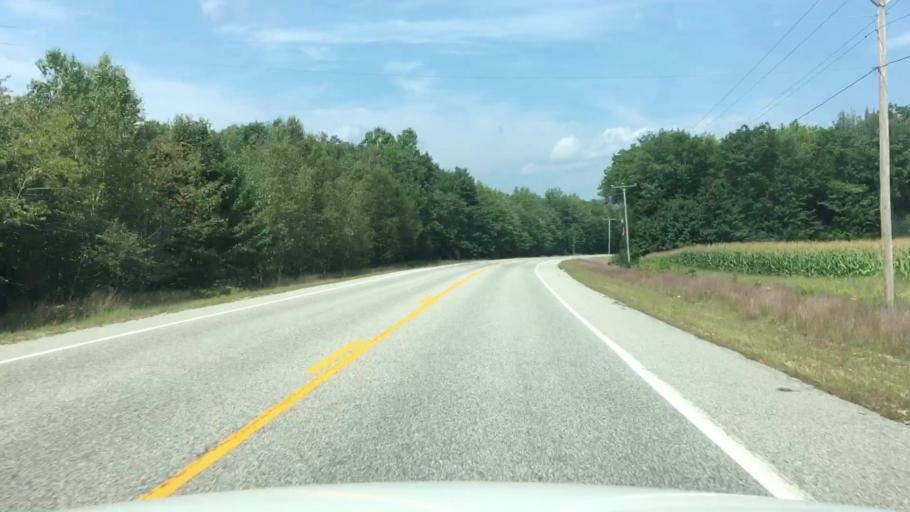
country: US
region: Maine
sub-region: Oxford County
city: Canton
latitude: 44.4719
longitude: -70.3256
